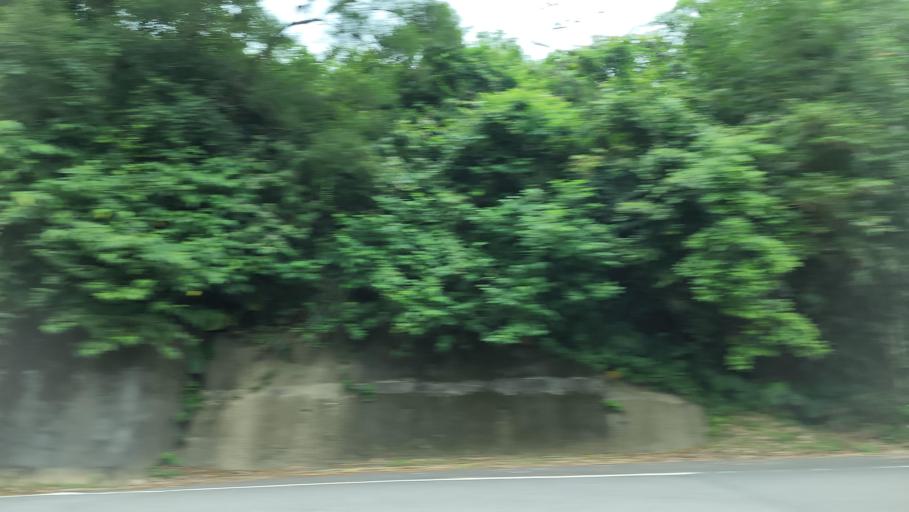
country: TW
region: Taiwan
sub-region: Keelung
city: Keelung
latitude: 25.1957
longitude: 121.6818
